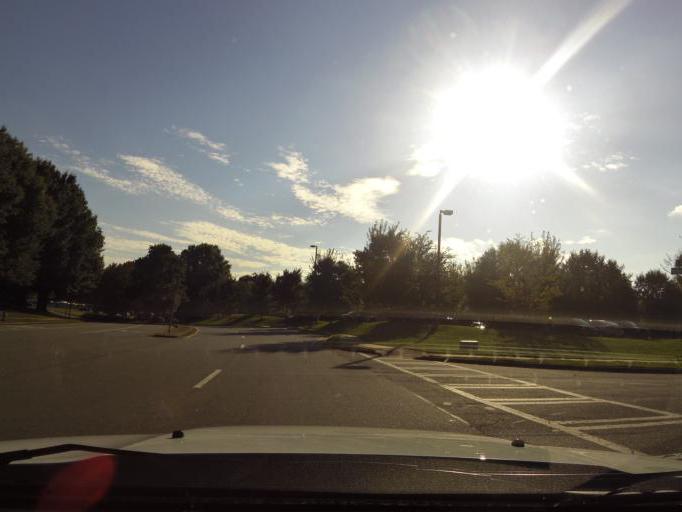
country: US
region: Georgia
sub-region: Cobb County
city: Kennesaw
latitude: 34.0039
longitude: -84.5959
